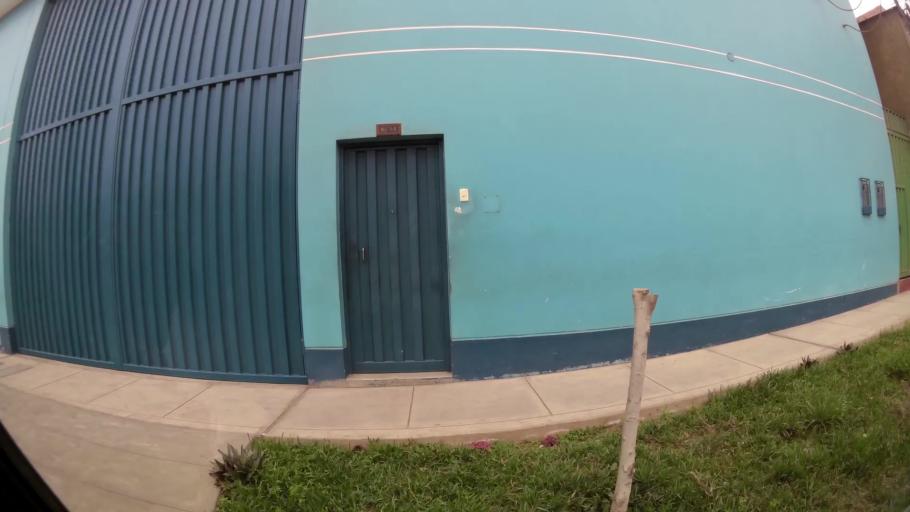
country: PE
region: Lima
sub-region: Lima
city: Urb. Santo Domingo
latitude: -11.8790
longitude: -77.0668
